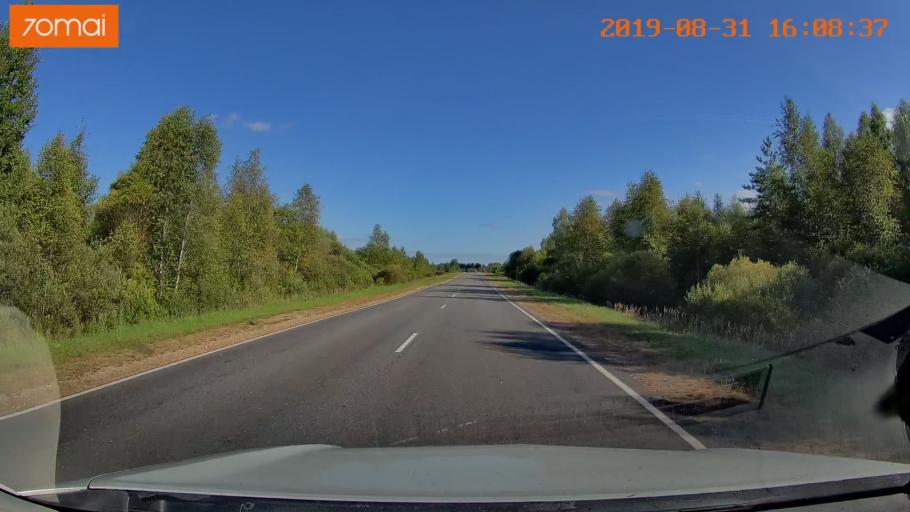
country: RU
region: Kaluga
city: Yukhnov
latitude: 54.5948
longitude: 35.3790
